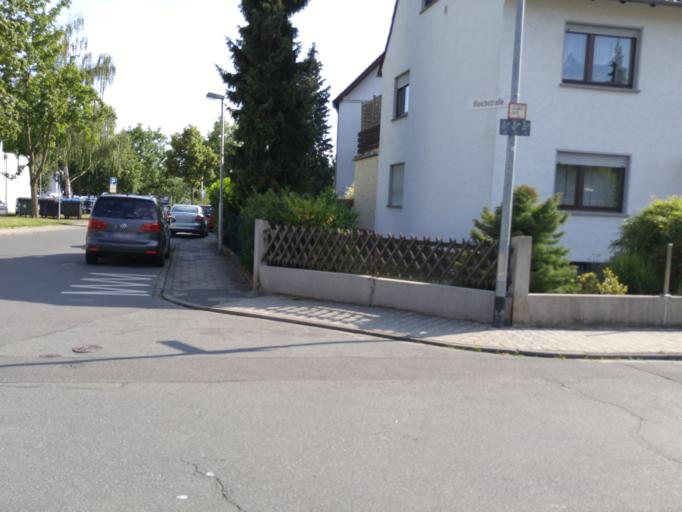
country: DE
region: Hesse
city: Langen
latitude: 49.9881
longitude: 8.6662
